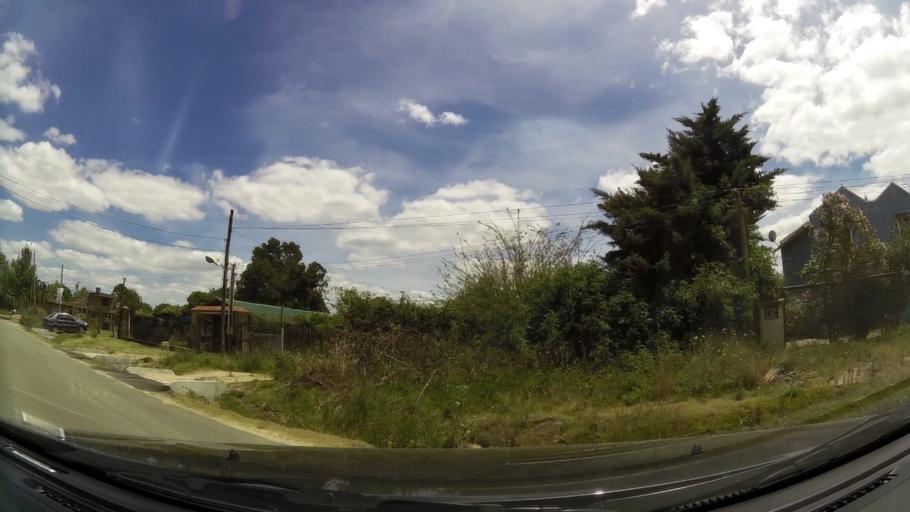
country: UY
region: Canelones
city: Colonia Nicolich
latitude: -34.8236
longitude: -55.9716
